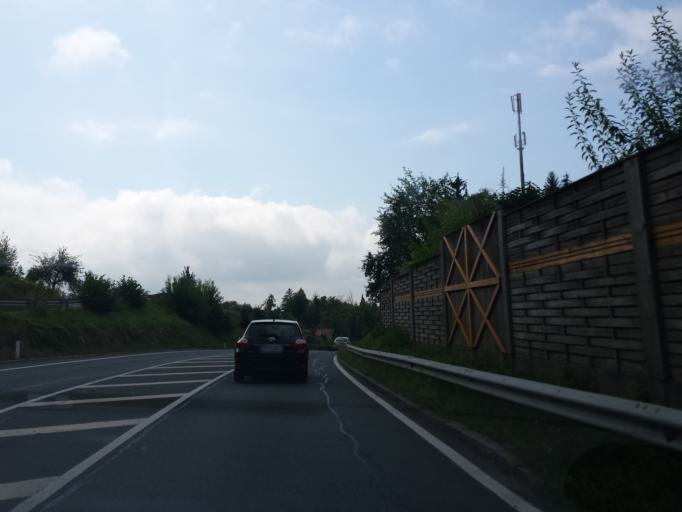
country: AT
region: Styria
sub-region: Politischer Bezirk Deutschlandsberg
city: Rassach
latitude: 46.8512
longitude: 15.2732
